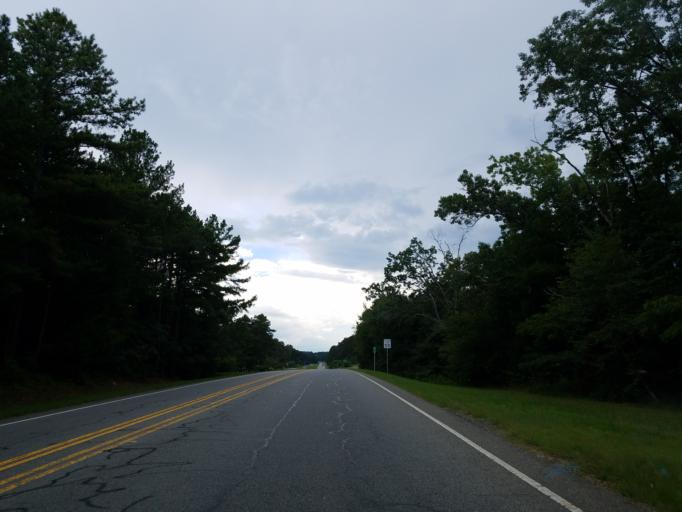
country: US
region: Georgia
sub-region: Bartow County
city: Adairsville
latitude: 34.2984
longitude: -84.8796
